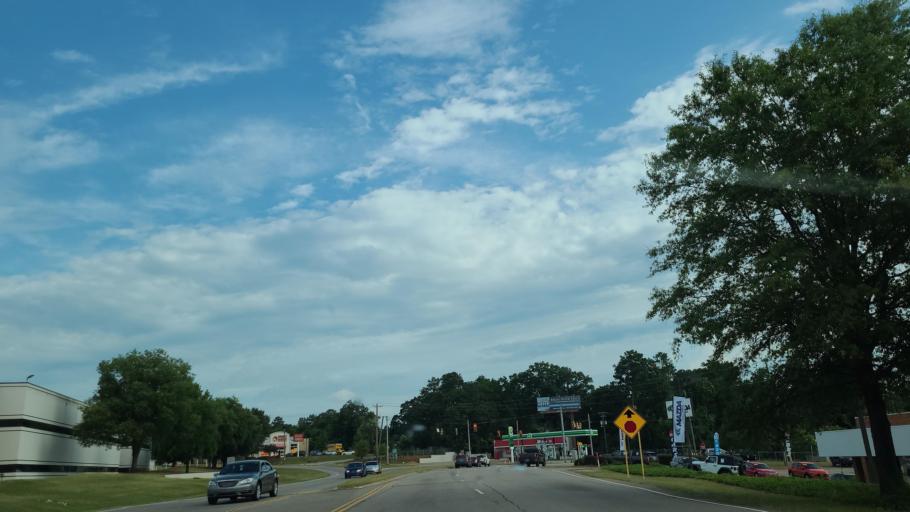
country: US
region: South Carolina
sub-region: Lexington County
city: West Columbia
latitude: 34.0238
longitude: -81.0784
